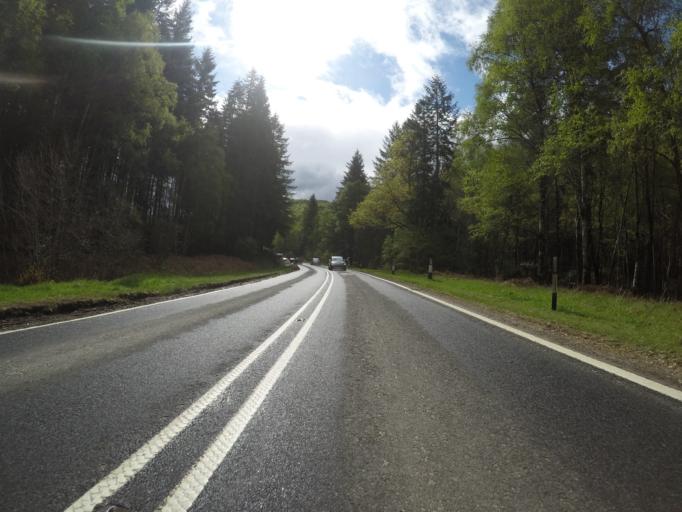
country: GB
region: Scotland
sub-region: Highland
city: Spean Bridge
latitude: 57.0666
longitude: -4.8315
